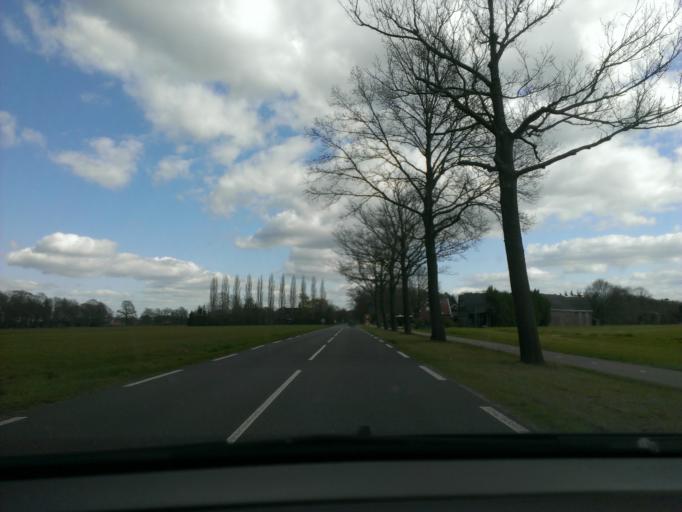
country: NL
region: Overijssel
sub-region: Gemeente Borne
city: Borne
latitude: 52.3106
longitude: 6.7069
